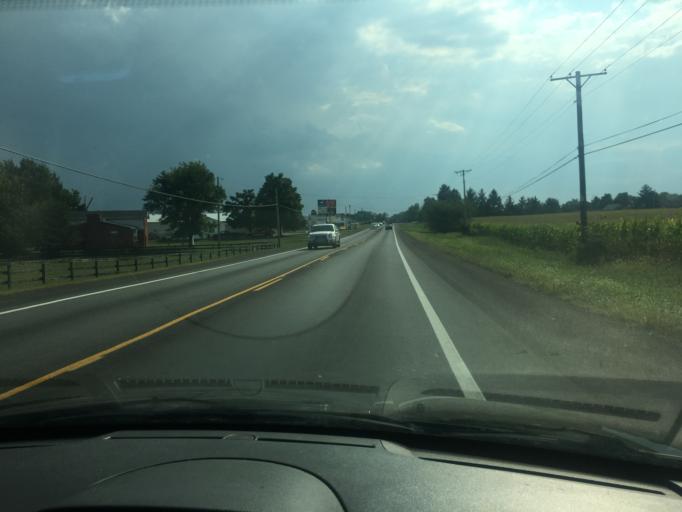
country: US
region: Ohio
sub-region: Champaign County
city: Urbana
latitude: 40.0825
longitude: -83.7612
